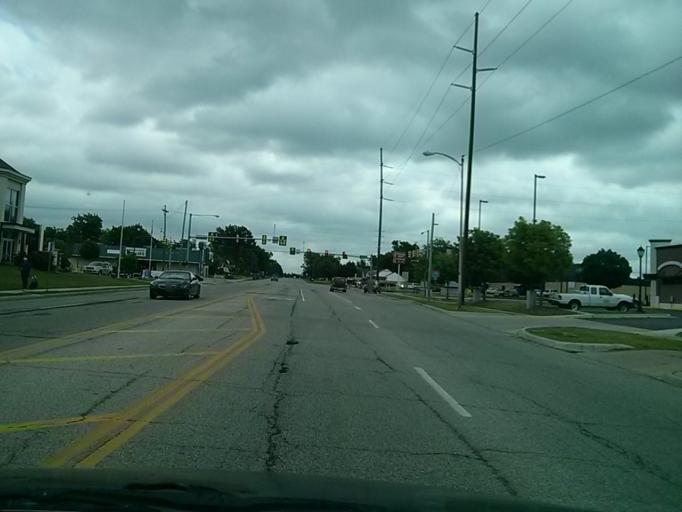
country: US
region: Oklahoma
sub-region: Tulsa County
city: Tulsa
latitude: 36.1566
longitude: -95.9595
